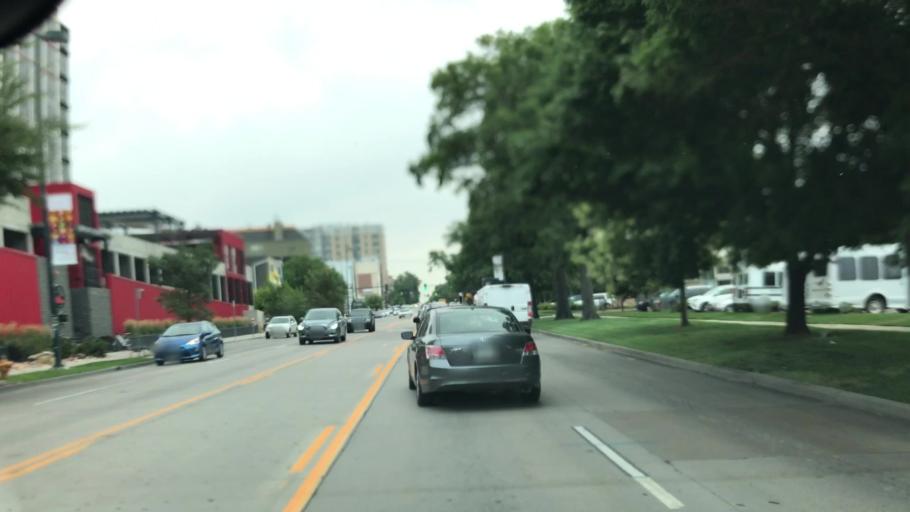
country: US
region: Colorado
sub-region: Arapahoe County
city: Glendale
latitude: 39.6818
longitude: -104.9594
